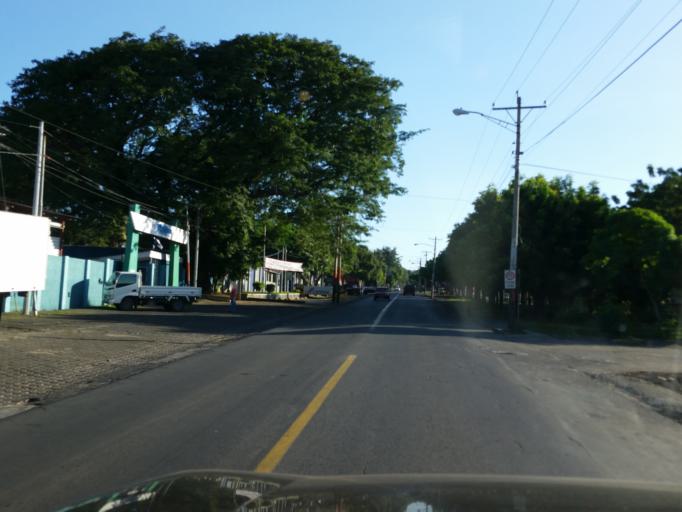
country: NI
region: Managua
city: Managua
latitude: 12.1366
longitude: -86.2990
